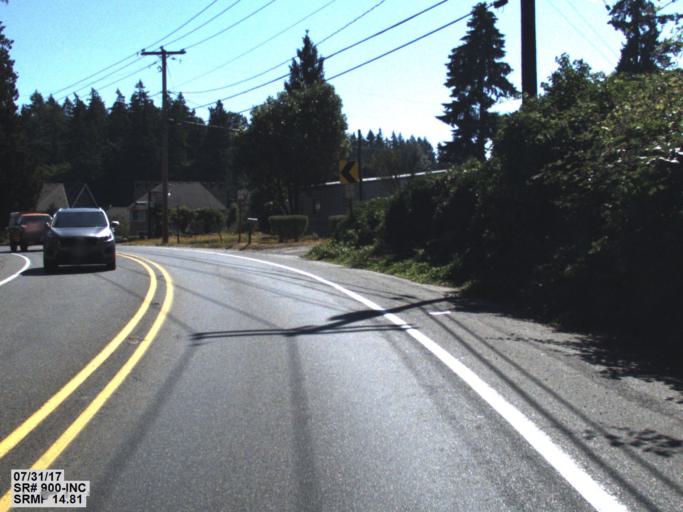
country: US
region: Washington
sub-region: King County
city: Newcastle
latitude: 47.5039
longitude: -122.1476
